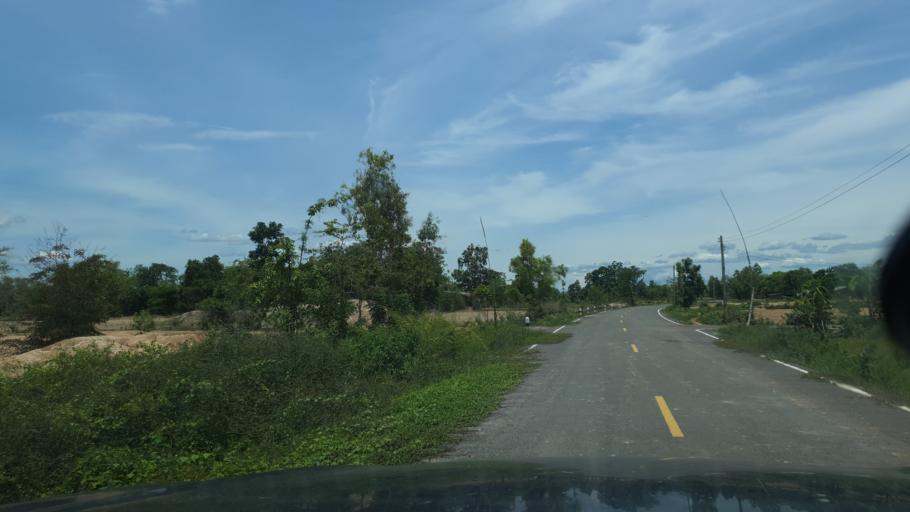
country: TH
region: Sukhothai
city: Ban Na
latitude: 17.1502
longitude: 99.6604
